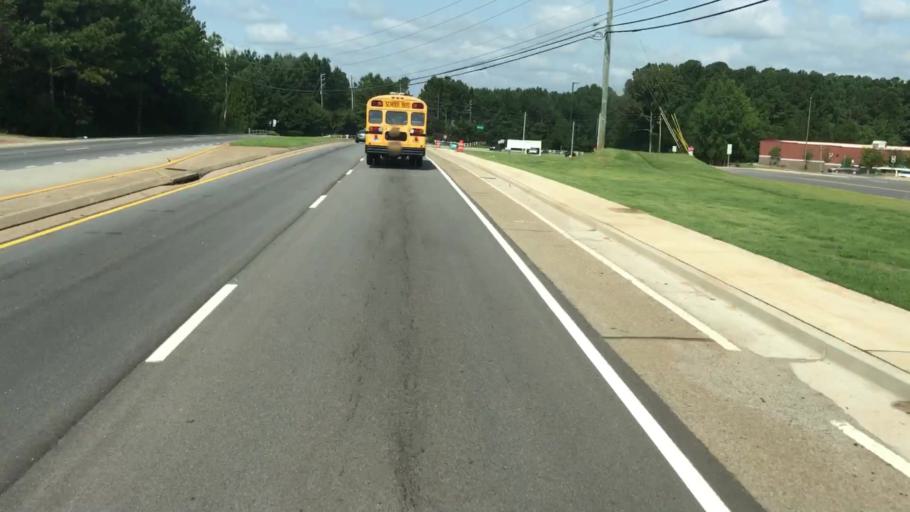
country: US
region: Georgia
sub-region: Gwinnett County
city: Lawrenceville
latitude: 33.9259
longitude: -84.0212
